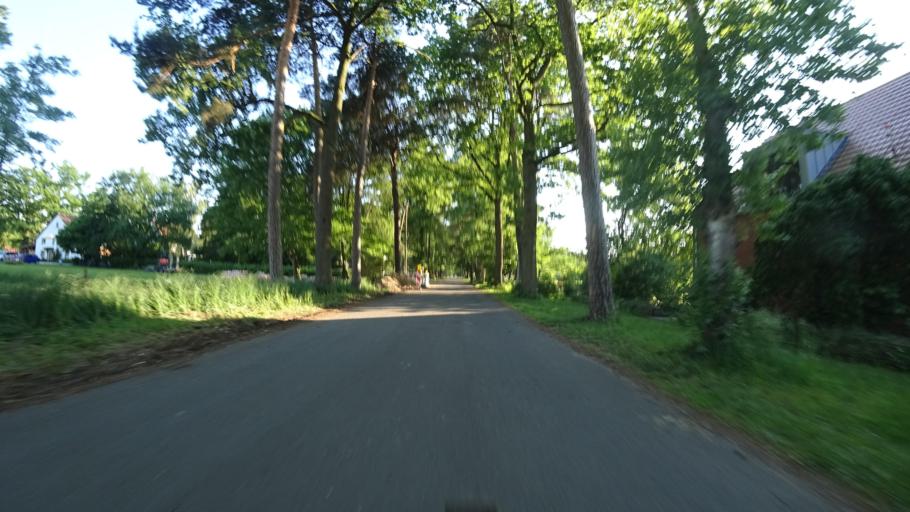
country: DE
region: North Rhine-Westphalia
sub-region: Regierungsbezirk Detmold
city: Guetersloh
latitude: 51.9334
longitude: 8.4049
